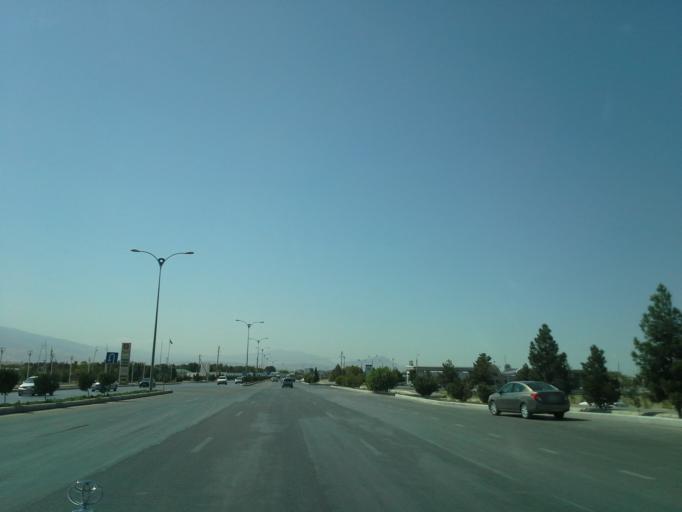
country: TM
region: Ahal
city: Annau
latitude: 37.9072
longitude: 58.5164
